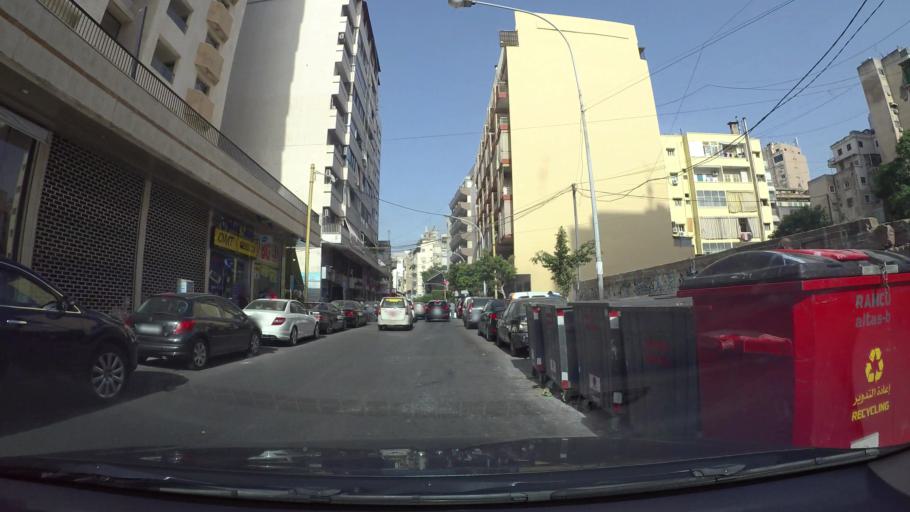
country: LB
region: Beyrouth
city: Ra's Bayrut
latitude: 33.8937
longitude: 35.4819
